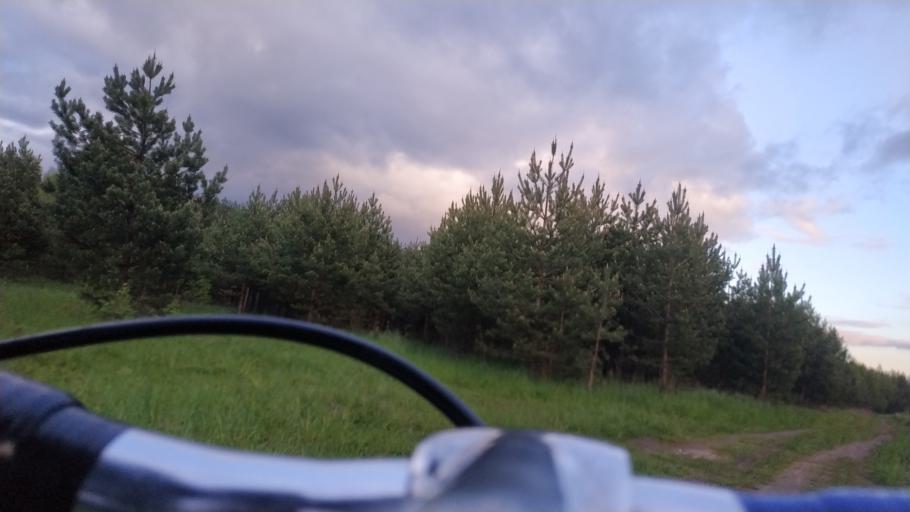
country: RU
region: Moskovskaya
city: Ramenskoye
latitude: 55.5936
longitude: 38.2889
